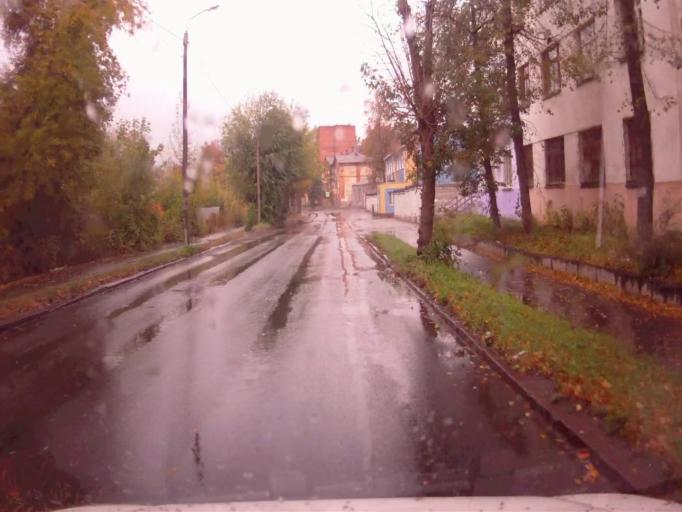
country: RU
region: Chelyabinsk
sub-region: Gorod Chelyabinsk
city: Chelyabinsk
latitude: 55.1941
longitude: 61.4110
